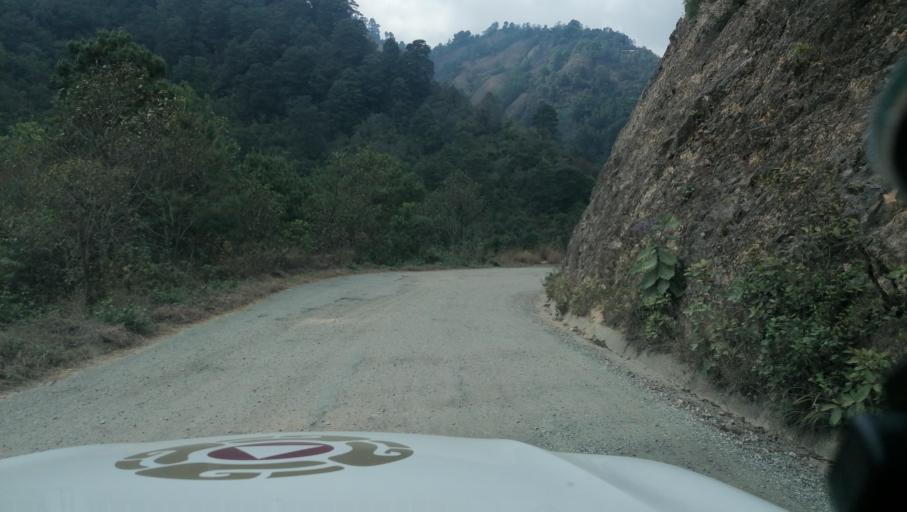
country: GT
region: San Marcos
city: Tacana
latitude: 15.2147
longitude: -92.2020
